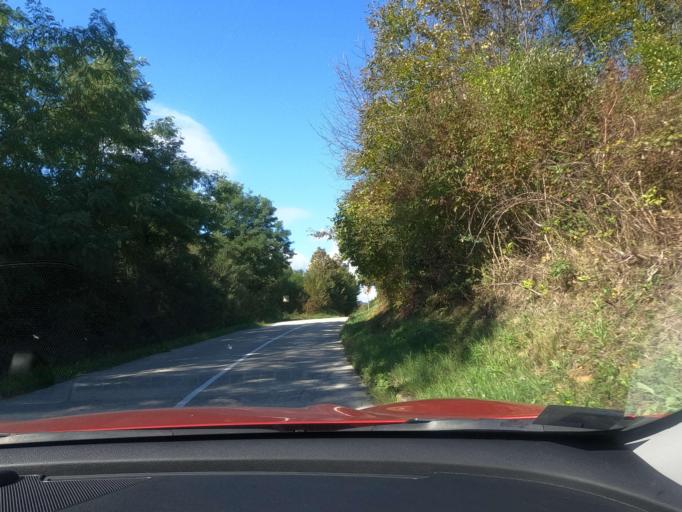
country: BA
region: Federation of Bosnia and Herzegovina
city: Podzvizd
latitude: 45.2298
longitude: 15.8906
